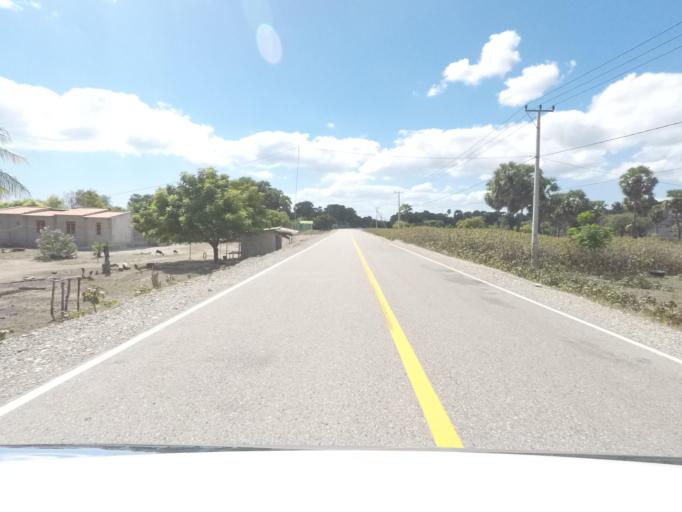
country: TL
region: Baucau
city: Baucau
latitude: -8.4341
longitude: 126.6723
